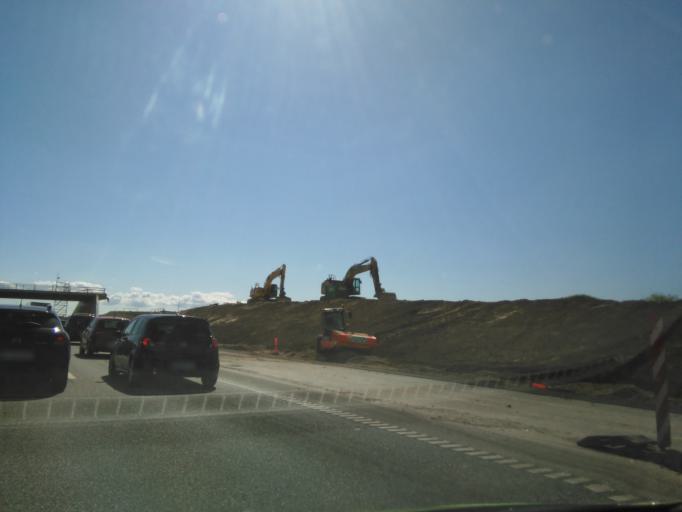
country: DK
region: Zealand
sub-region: Solrod Kommune
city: Solrod
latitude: 55.5063
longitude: 12.1767
